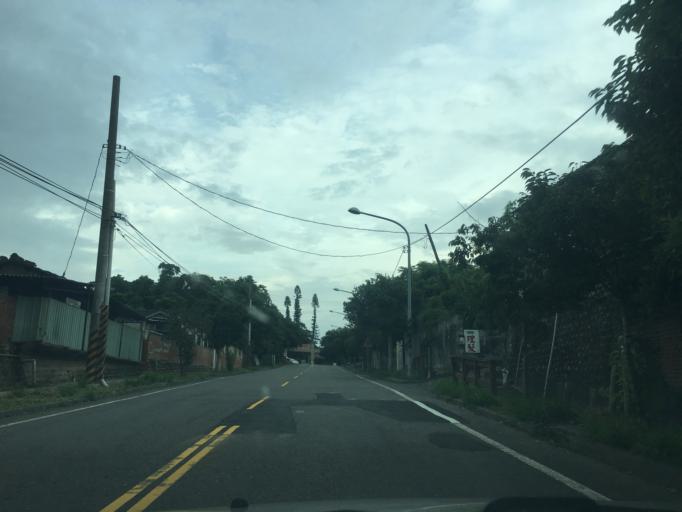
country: TW
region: Taiwan
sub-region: Changhua
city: Chang-hua
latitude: 24.0714
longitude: 120.5638
